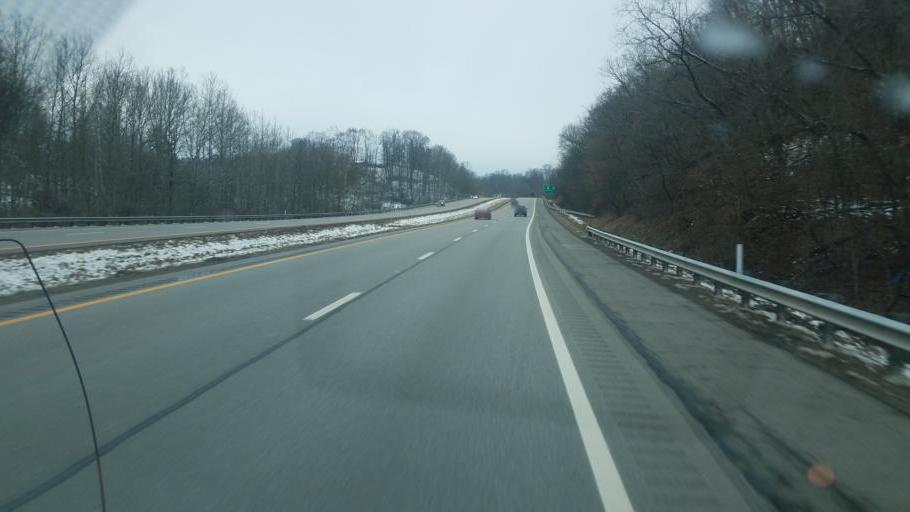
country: US
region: West Virginia
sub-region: Wood County
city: Boaz
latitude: 39.3424
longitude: -81.4549
